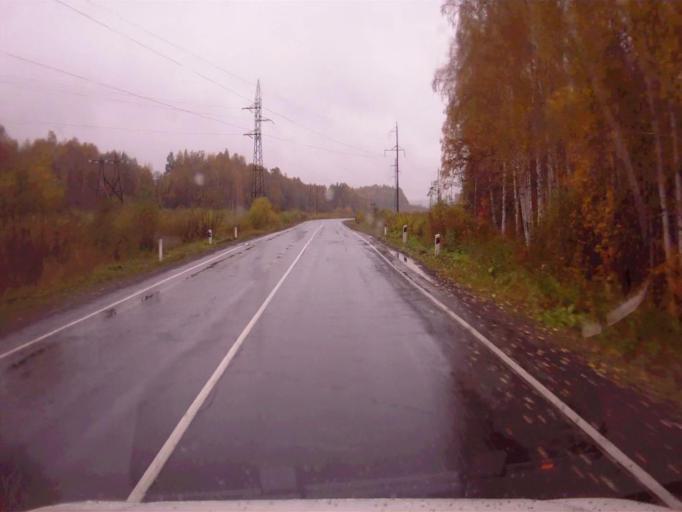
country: RU
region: Chelyabinsk
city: Verkhniy Ufaley
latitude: 55.9444
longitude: 60.4068
